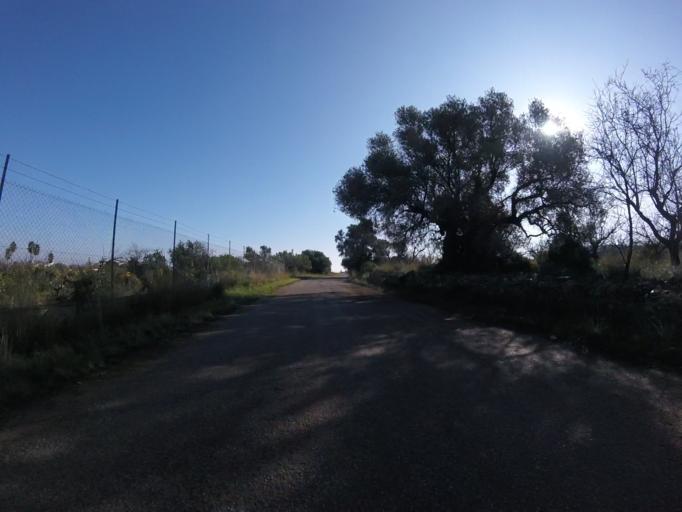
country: ES
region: Valencia
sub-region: Provincia de Castello
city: Peniscola
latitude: 40.3891
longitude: 0.3714
